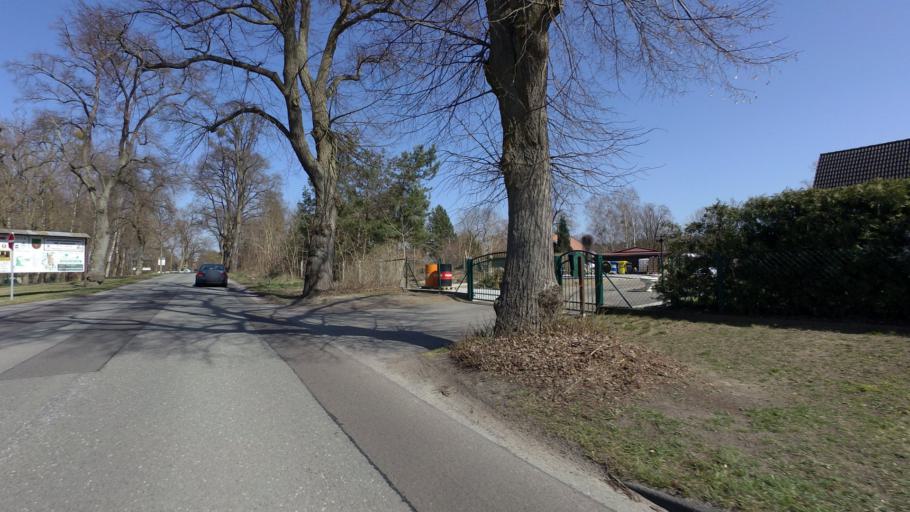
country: DE
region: Brandenburg
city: Lindow
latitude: 52.9614
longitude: 12.9824
